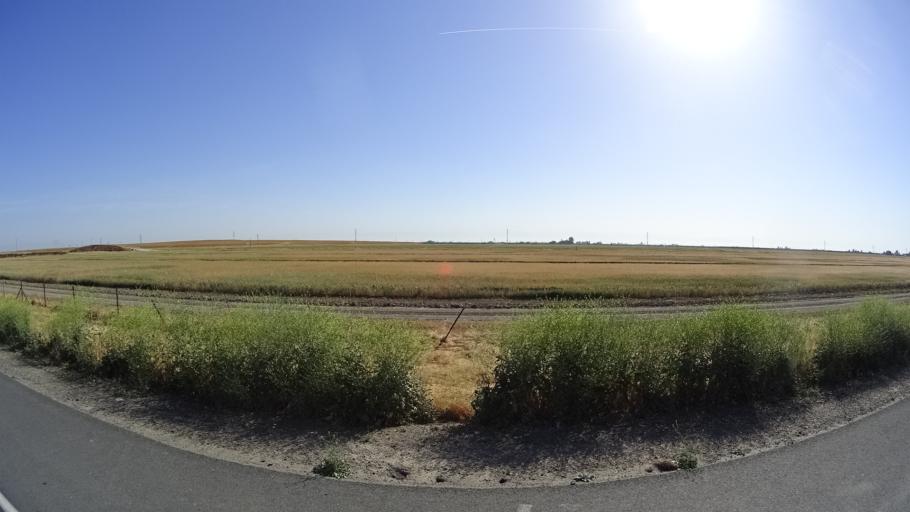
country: US
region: California
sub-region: Kings County
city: Corcoran
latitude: 36.1278
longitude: -119.5779
